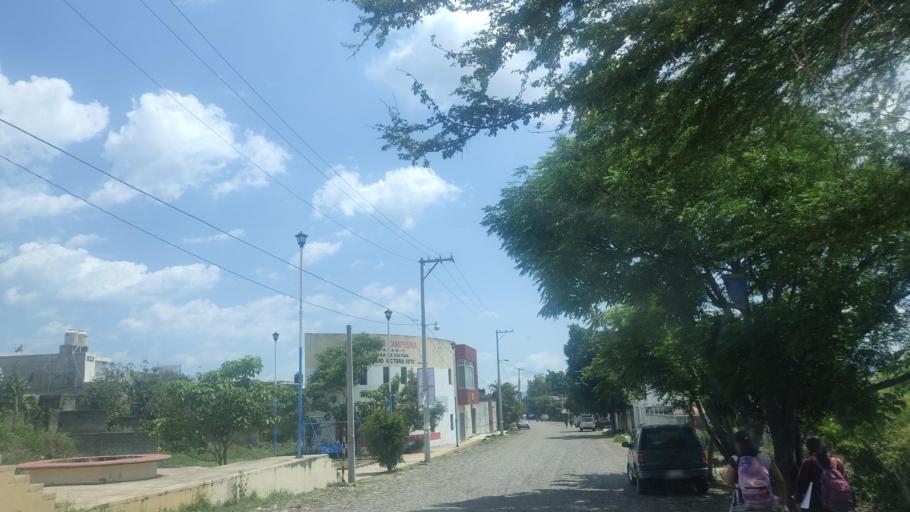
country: MX
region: Nayarit
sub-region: Tepic
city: La Corregidora
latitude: 21.4457
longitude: -104.8104
